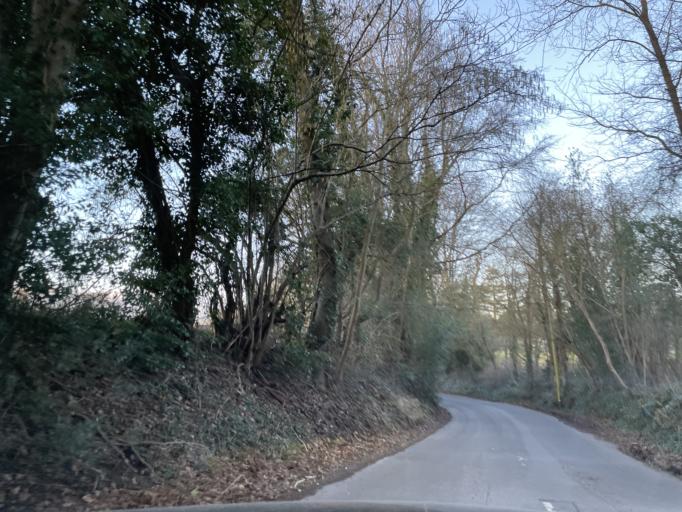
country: GB
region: England
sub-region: Kent
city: Halstead
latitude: 51.2730
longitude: 0.1269
